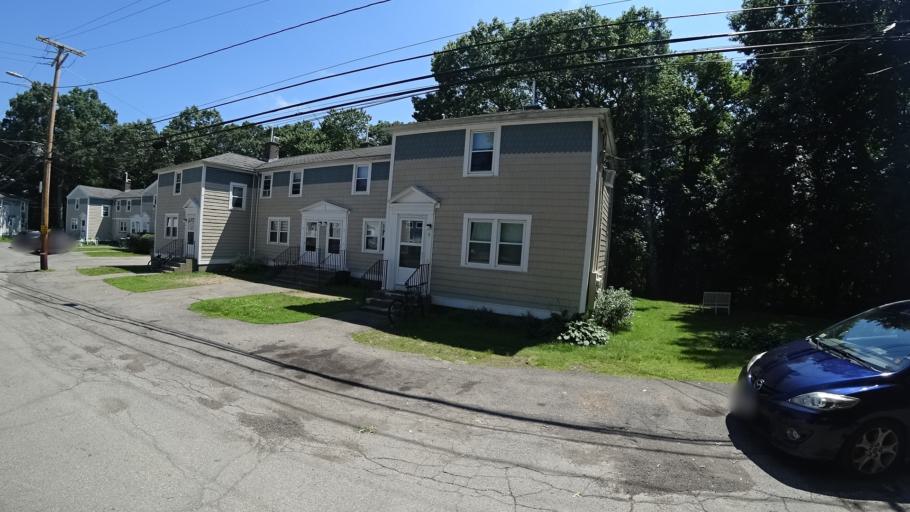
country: US
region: Massachusetts
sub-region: Norfolk County
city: Dedham
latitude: 42.2453
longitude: -71.1481
